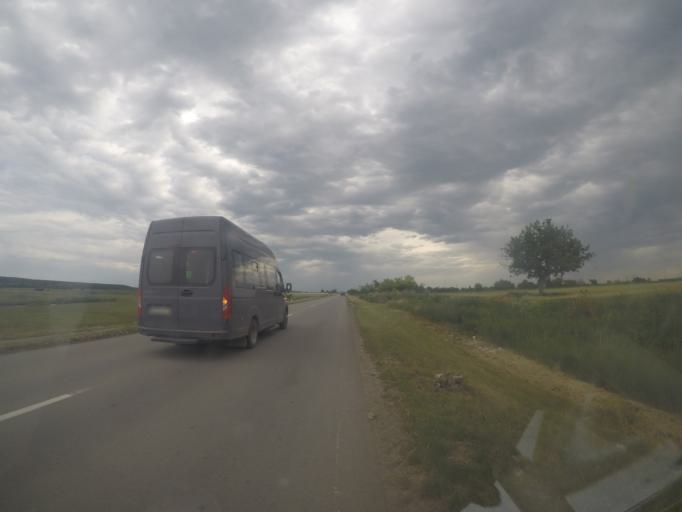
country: RS
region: Autonomna Pokrajina Vojvodina
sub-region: Juznobanatski Okrug
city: Opovo
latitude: 45.0629
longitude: 20.4362
